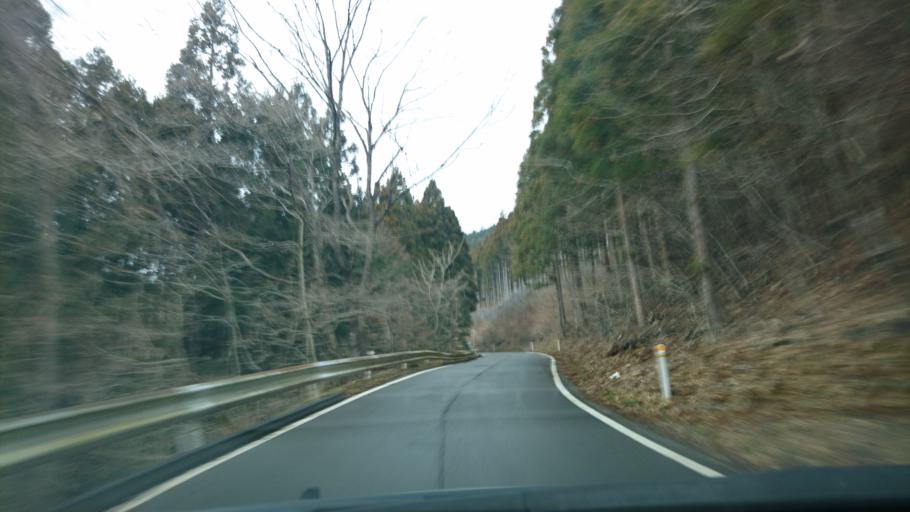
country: JP
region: Iwate
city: Ofunato
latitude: 38.9886
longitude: 141.5523
